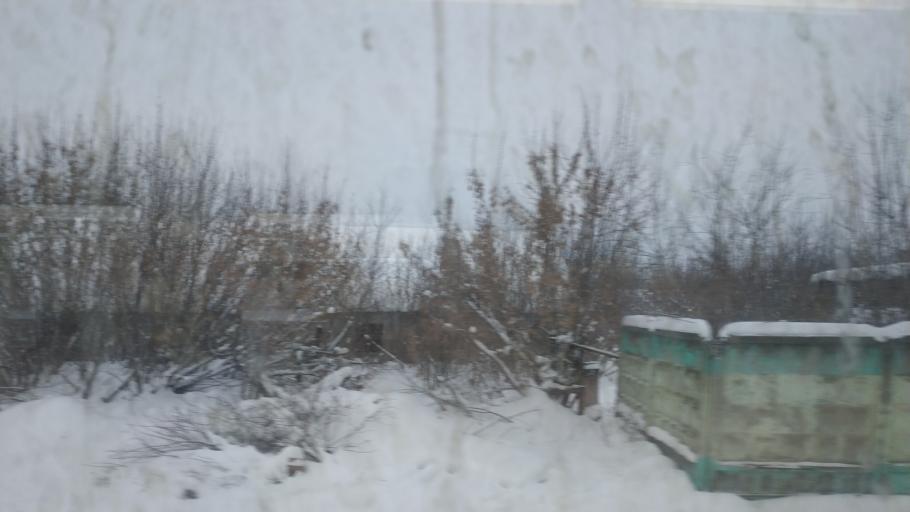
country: RU
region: Moskovskaya
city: Ramenskoye
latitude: 55.5566
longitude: 38.2504
